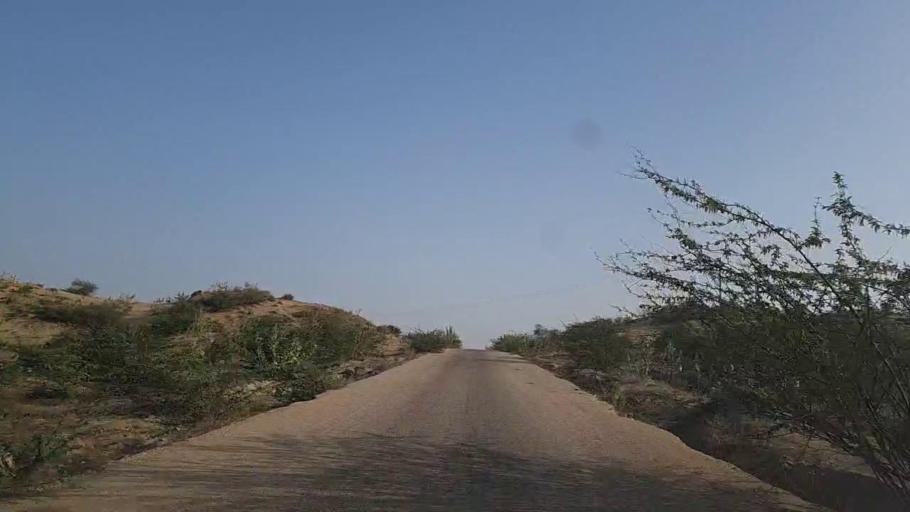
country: PK
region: Sindh
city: Diplo
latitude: 24.6080
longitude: 69.3780
